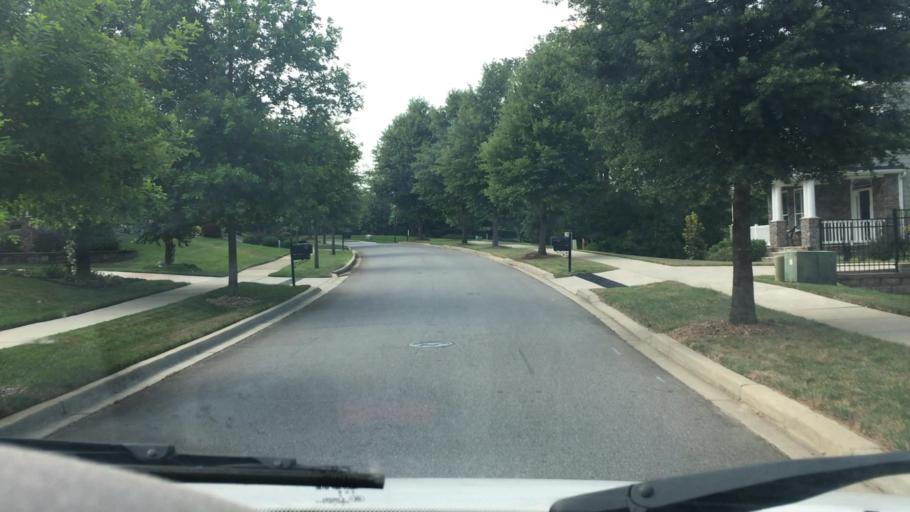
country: US
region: North Carolina
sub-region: Mecklenburg County
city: Huntersville
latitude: 35.4118
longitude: -80.8232
